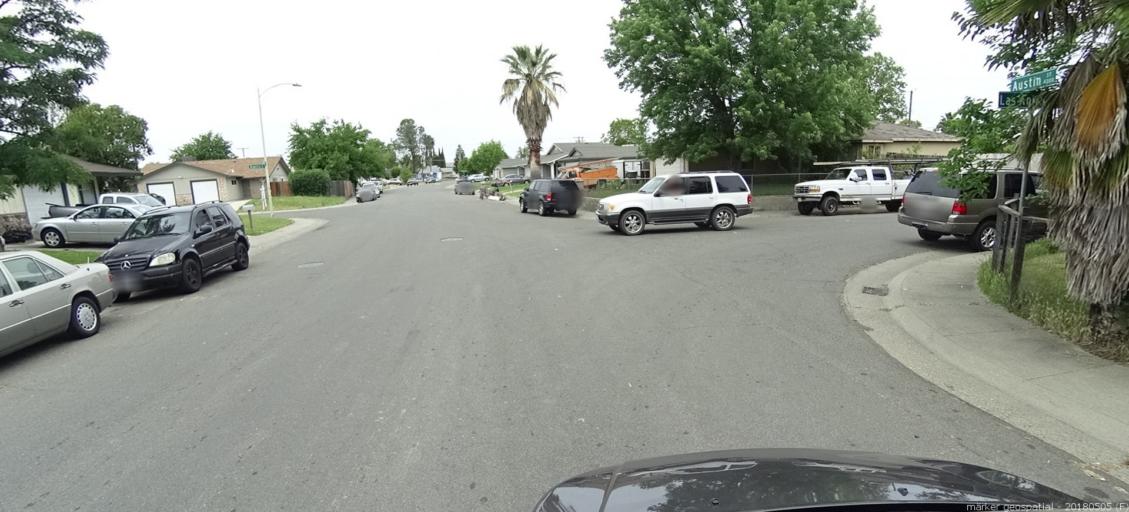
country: US
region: California
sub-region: Sacramento County
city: Rio Linda
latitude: 38.6460
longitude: -121.4611
